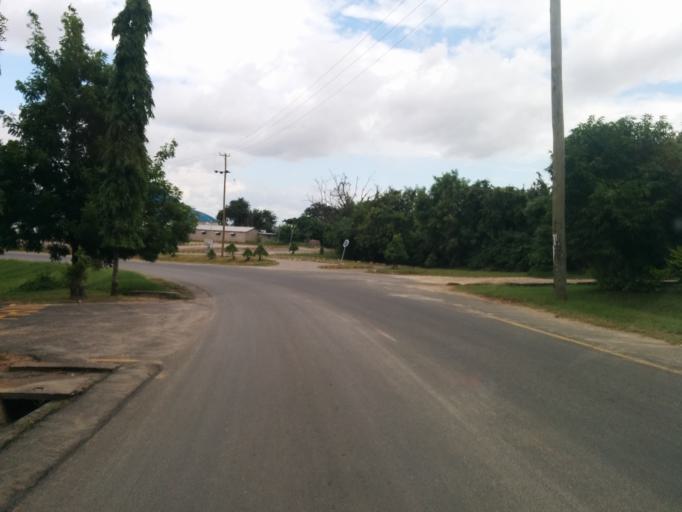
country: TZ
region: Dar es Salaam
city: Magomeni
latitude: -6.7817
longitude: 39.2025
